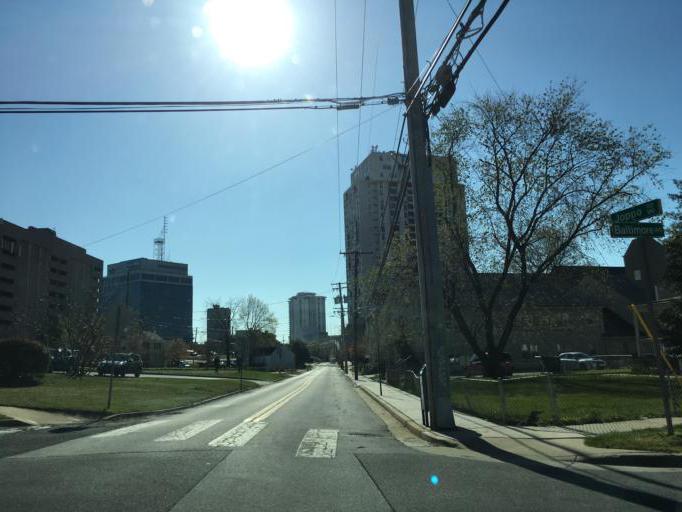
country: US
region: Maryland
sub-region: Baltimore County
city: Towson
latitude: 39.4032
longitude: -76.6069
